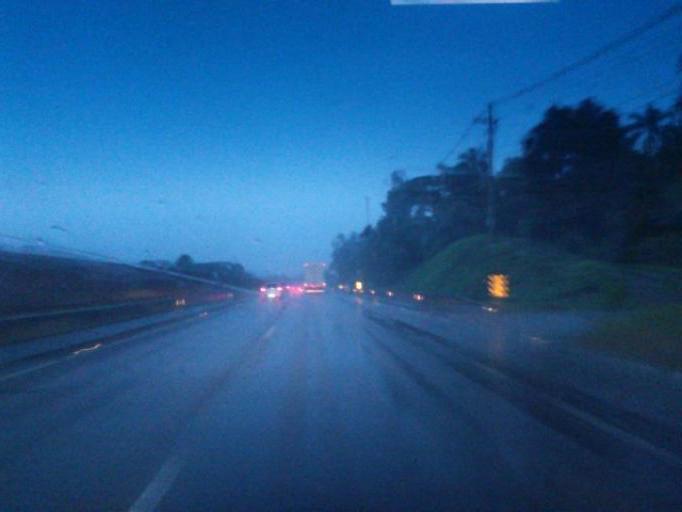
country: BR
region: Sao Paulo
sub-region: Juquitiba
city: Juquitiba
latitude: -23.9382
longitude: -47.0384
